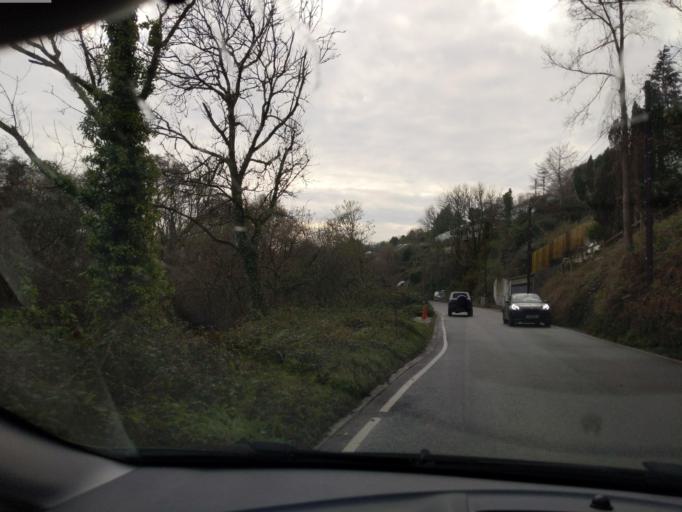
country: GB
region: England
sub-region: Cornwall
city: Looe
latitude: 50.3700
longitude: -4.3885
